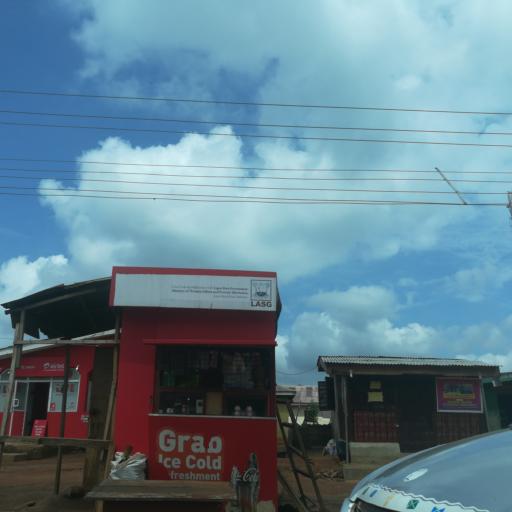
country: NG
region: Lagos
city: Ejirin
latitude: 6.6482
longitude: 3.7130
